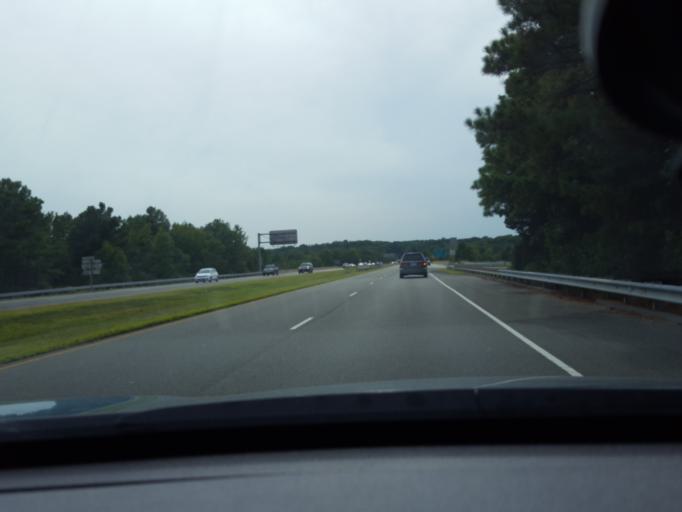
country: US
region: Virginia
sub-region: Henrico County
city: Chamberlayne
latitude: 37.6459
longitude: -77.4114
